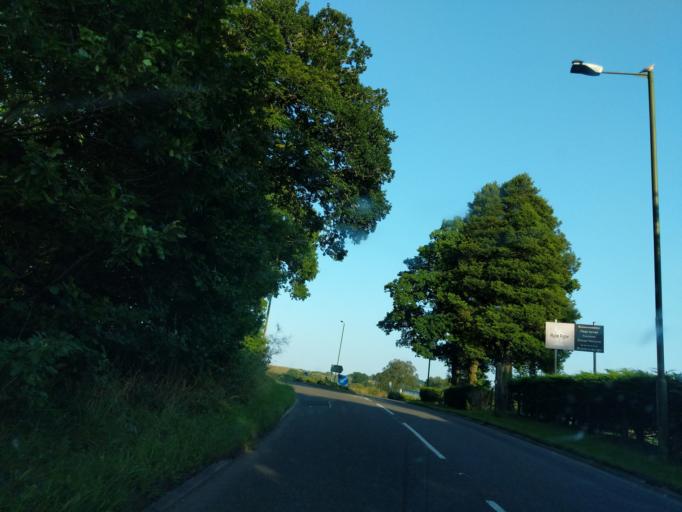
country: GB
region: Scotland
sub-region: Stirling
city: Balfron
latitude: 56.1724
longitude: -4.3672
